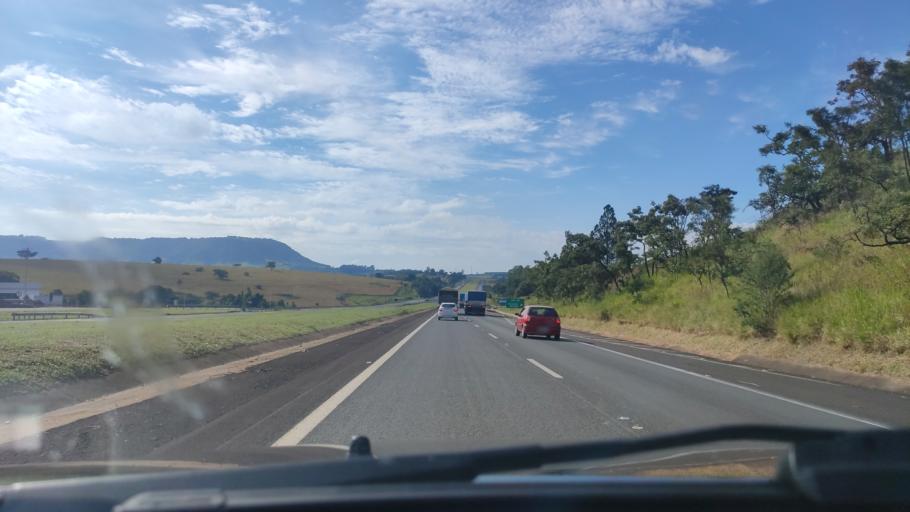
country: BR
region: Sao Paulo
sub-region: Itatinga
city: Itatinga
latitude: -23.1472
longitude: -48.4014
